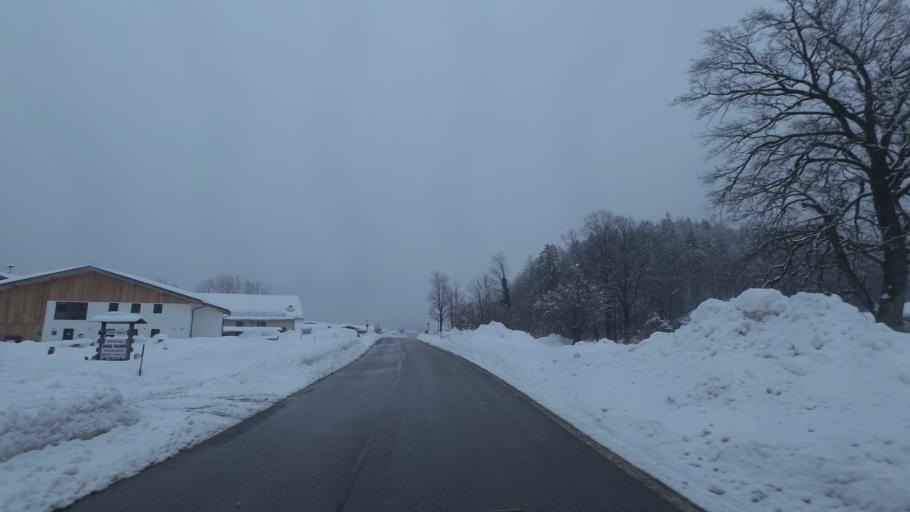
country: DE
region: Bavaria
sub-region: Upper Bavaria
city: Schleching
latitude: 47.7248
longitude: 12.4069
